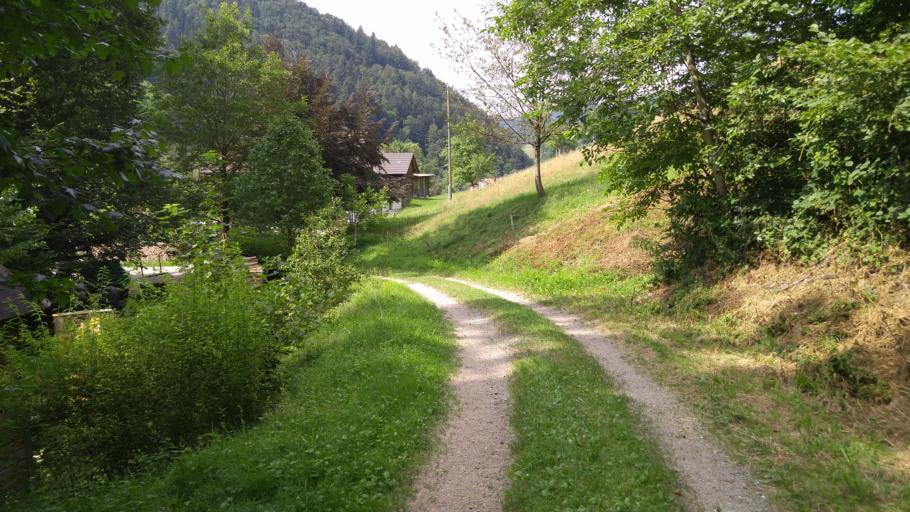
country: DE
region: Baden-Wuerttemberg
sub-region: Freiburg Region
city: Muenstertal/Schwarzwald
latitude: 47.8367
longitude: 7.7948
